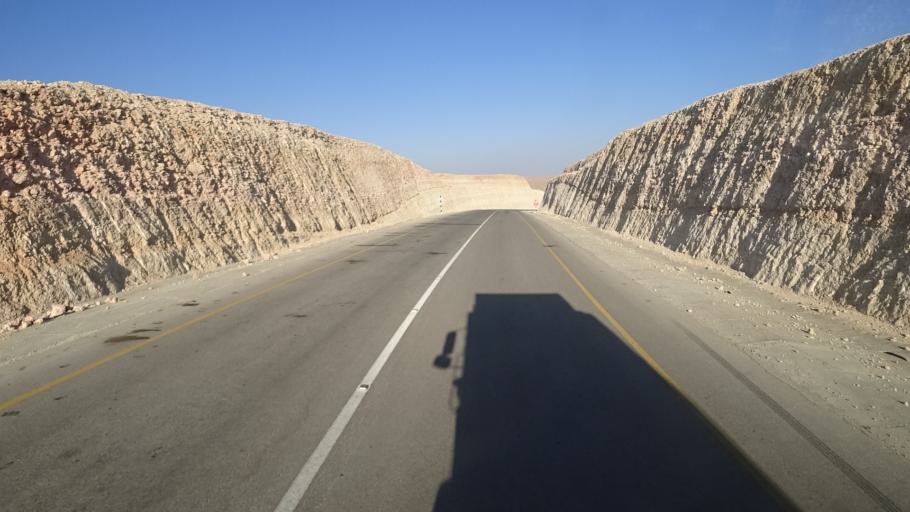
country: YE
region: Al Mahrah
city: Hawf
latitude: 17.0905
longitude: 53.0374
